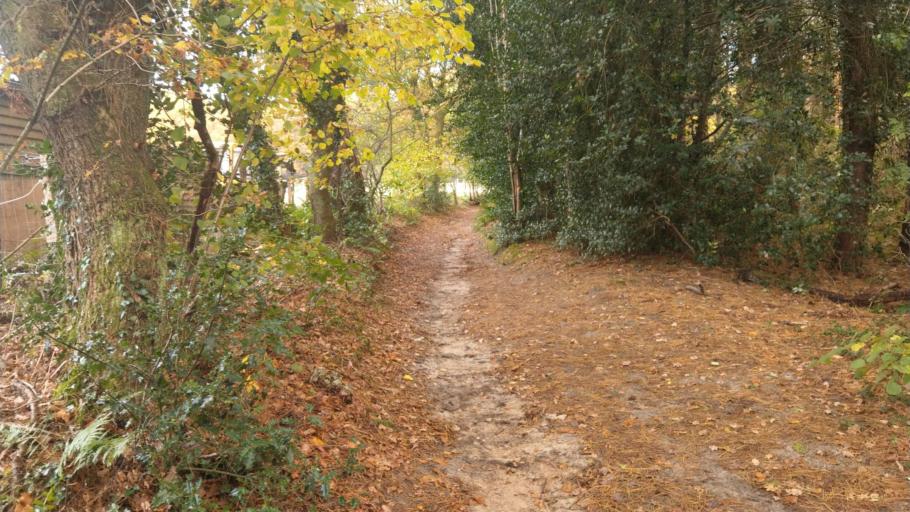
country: BE
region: Wallonia
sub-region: Province de Liege
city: La Calamine
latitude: 50.7310
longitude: 6.0075
